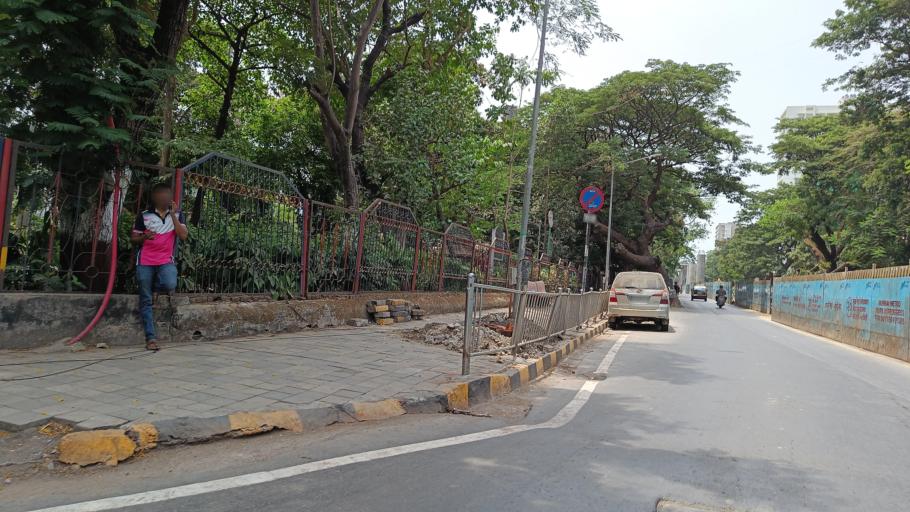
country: IN
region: Maharashtra
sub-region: Mumbai Suburban
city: Mumbai
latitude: 19.0738
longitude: 72.8376
